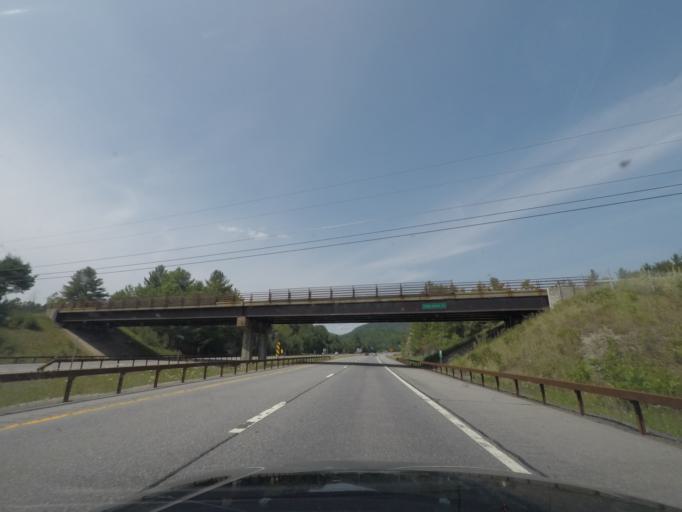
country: US
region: New York
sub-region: Warren County
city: Warrensburg
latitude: 43.7356
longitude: -73.8252
